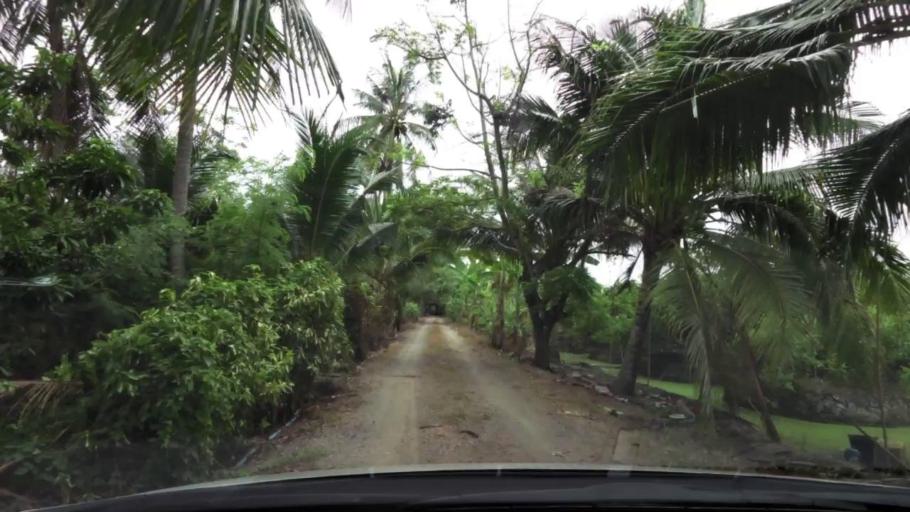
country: TH
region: Ratchaburi
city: Damnoen Saduak
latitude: 13.5701
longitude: 100.0036
